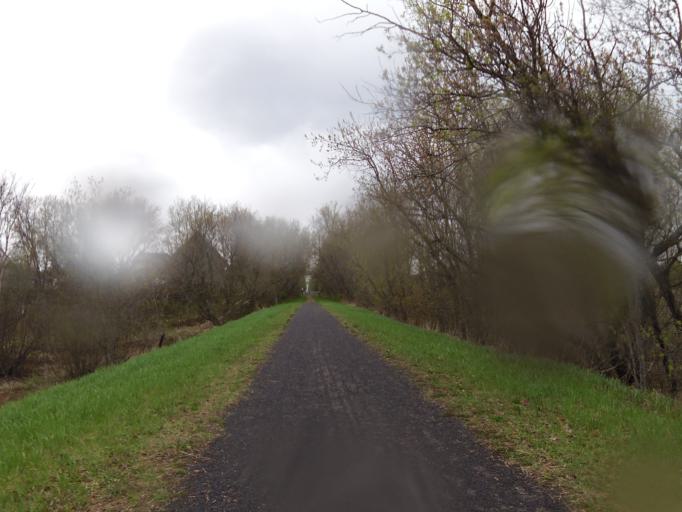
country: CA
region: Ontario
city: Bourget
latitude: 45.4339
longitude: -75.2518
